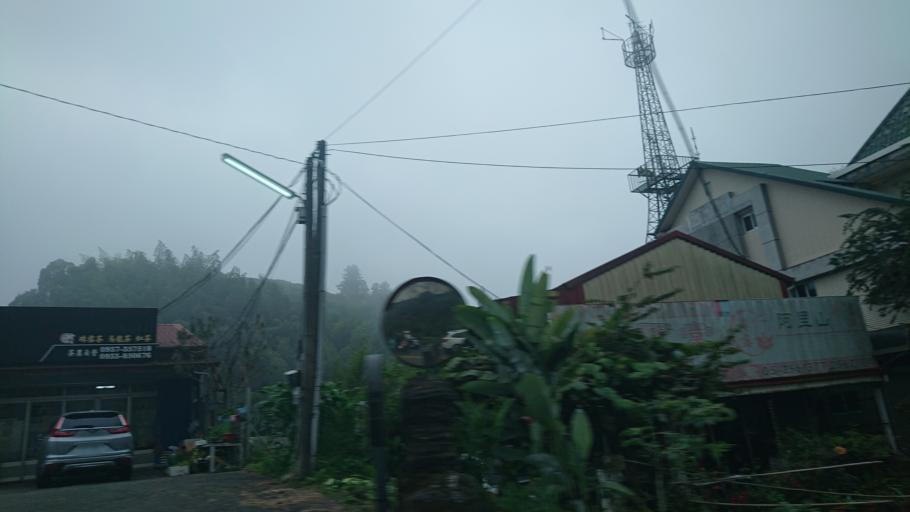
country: TW
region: Taiwan
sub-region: Chiayi
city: Jiayi Shi
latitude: 23.4730
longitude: 120.6983
